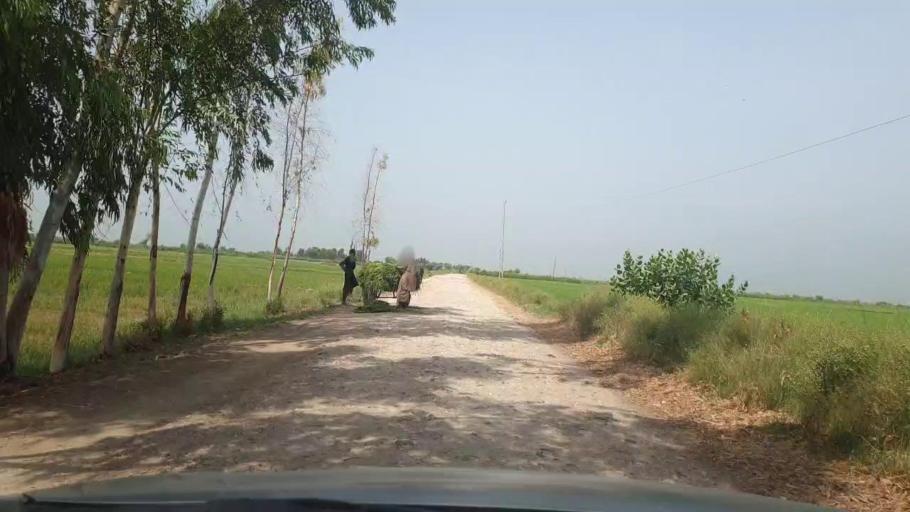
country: PK
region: Sindh
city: Garhi Yasin
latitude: 27.9089
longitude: 68.3950
